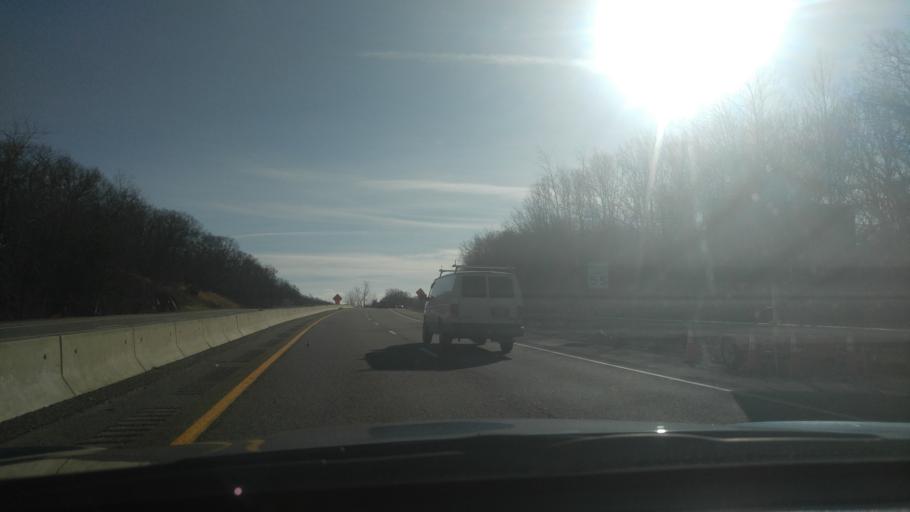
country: US
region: Rhode Island
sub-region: Providence County
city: Cumberland Hill
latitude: 41.9596
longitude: -71.4833
